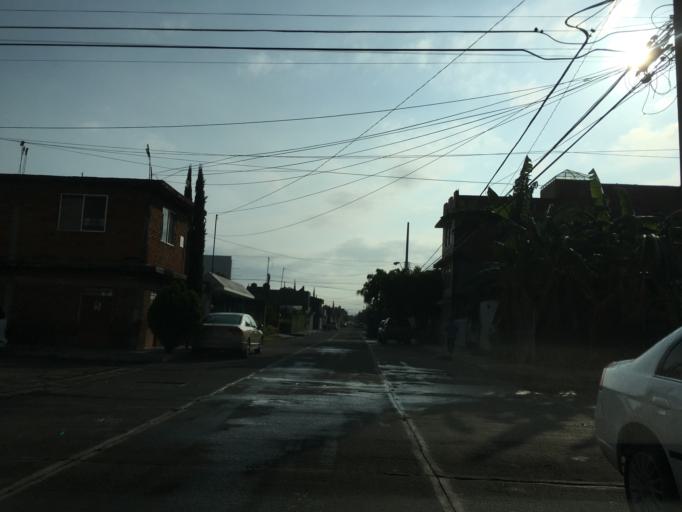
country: MX
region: Michoacan
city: Morelia
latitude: 19.6921
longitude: -101.2213
